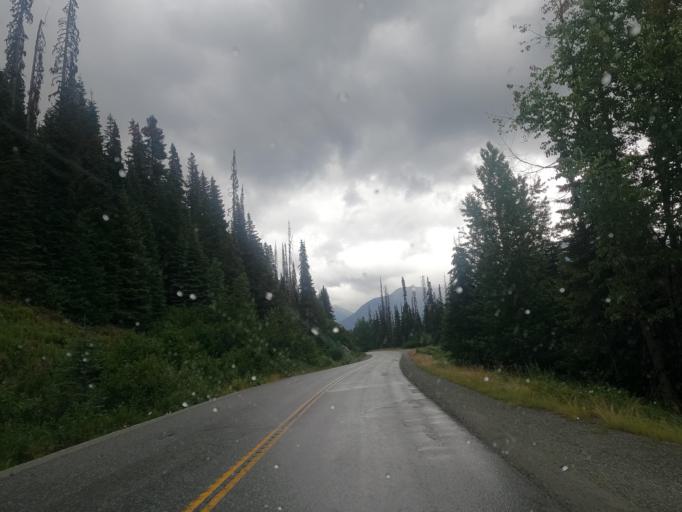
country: CA
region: British Columbia
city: Pemberton
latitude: 50.3861
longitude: -122.4484
